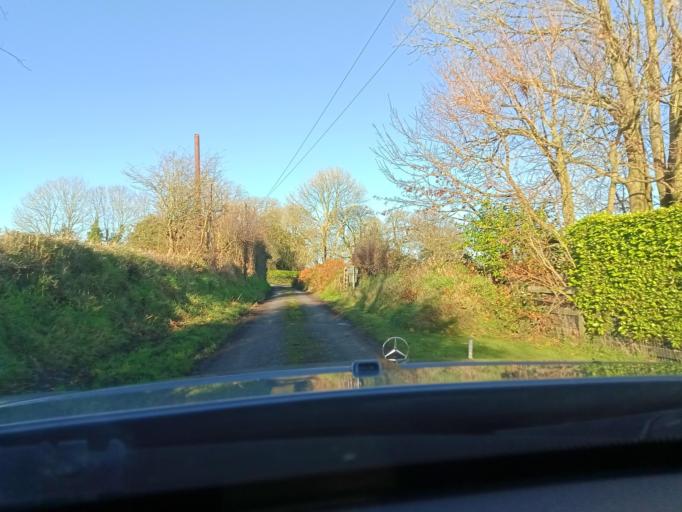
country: IE
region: Leinster
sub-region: Kilkenny
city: Mooncoin
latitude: 52.2986
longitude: -7.2080
